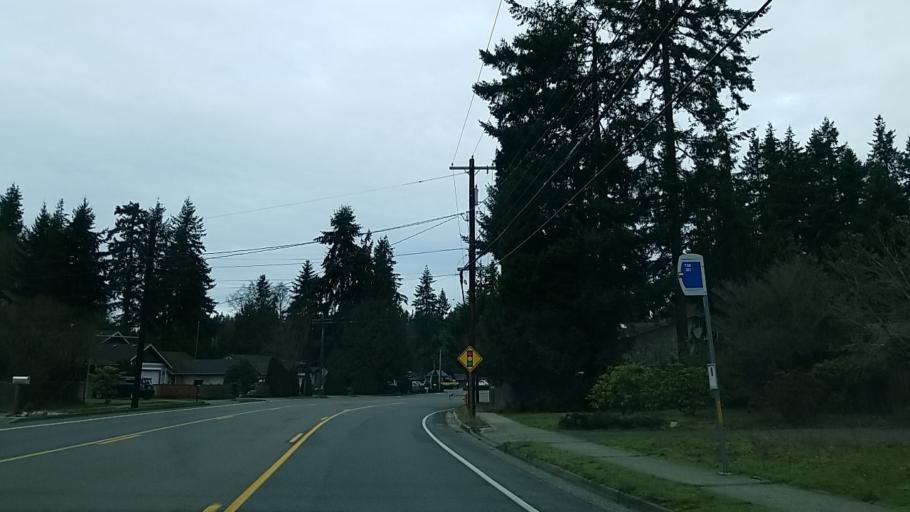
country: US
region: Washington
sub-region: Snohomish County
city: Esperance
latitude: 47.7811
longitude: -122.3661
